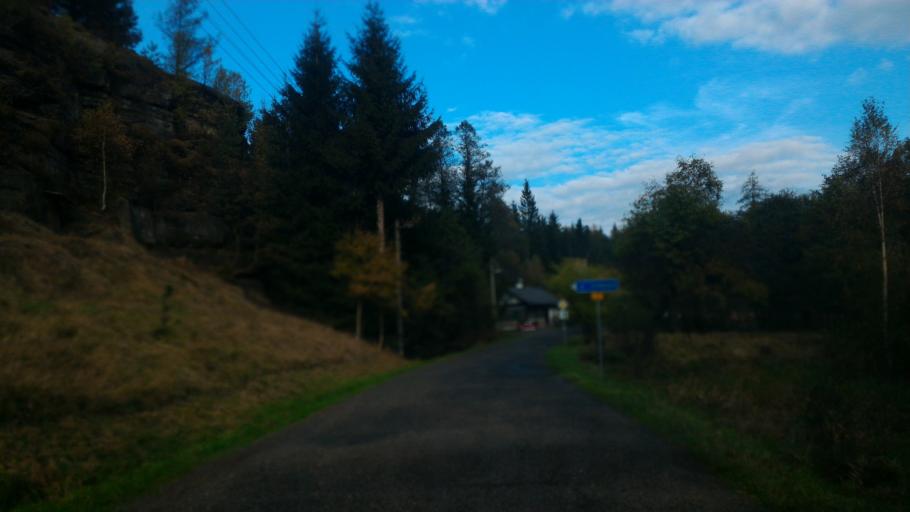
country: CZ
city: Kamenicky Senov
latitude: 50.8105
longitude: 14.4835
